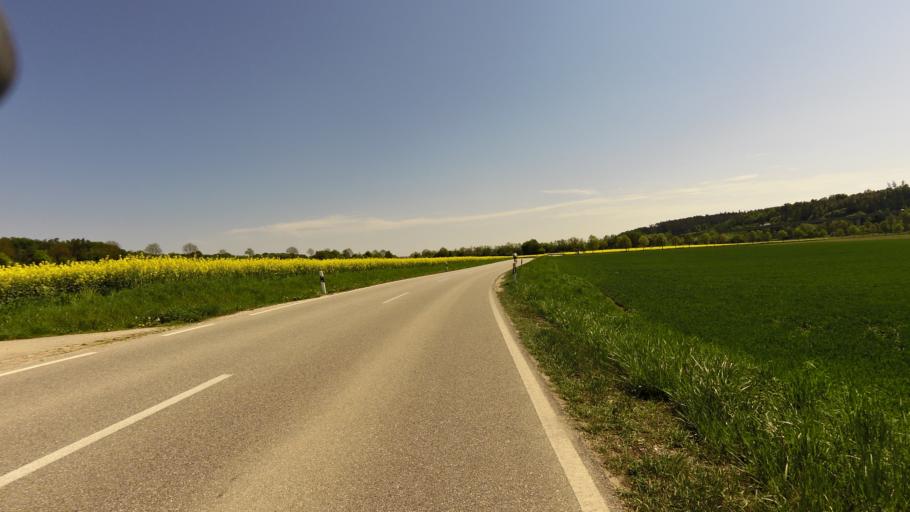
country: DE
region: Bavaria
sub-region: Lower Bavaria
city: Weihmichl
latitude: 48.5710
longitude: 12.0845
